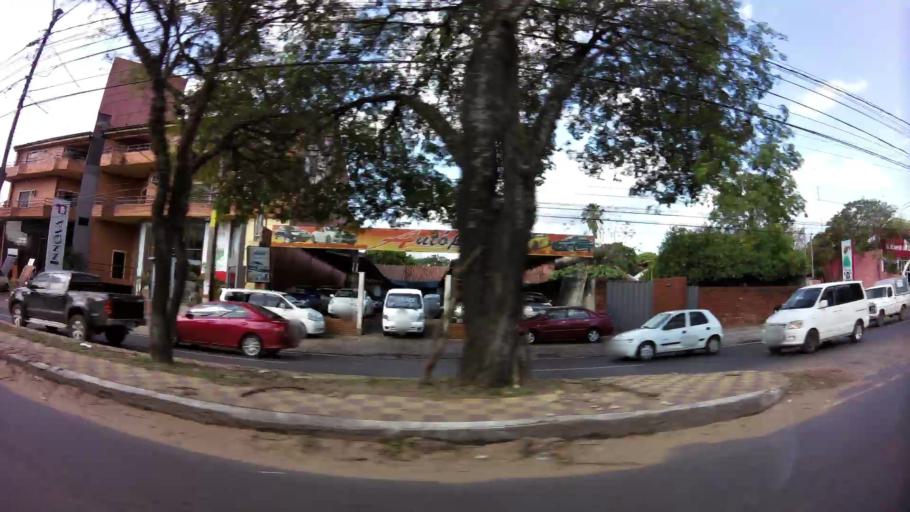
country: PY
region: Central
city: Fernando de la Mora
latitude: -25.3125
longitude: -57.5296
